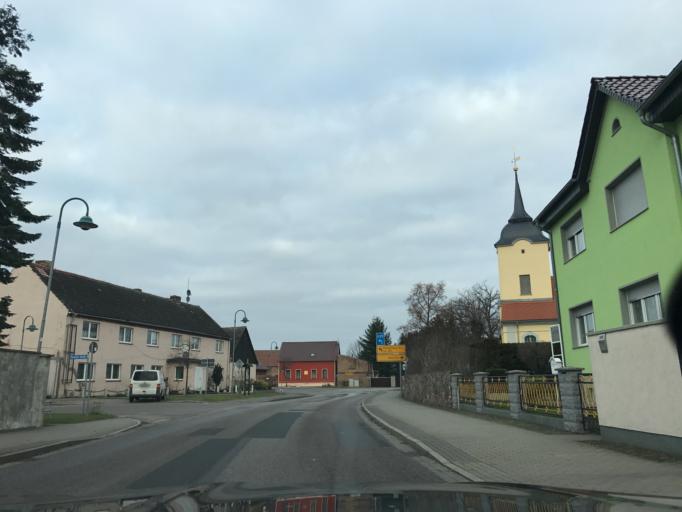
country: DE
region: Brandenburg
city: Golzow
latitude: 52.3508
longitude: 12.6287
